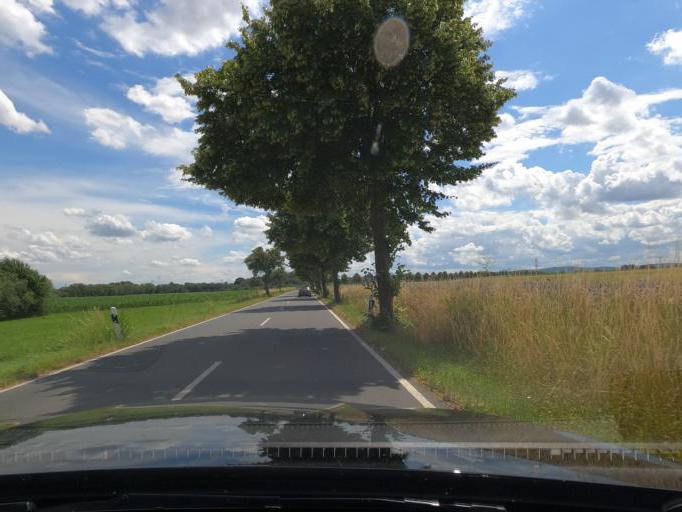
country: DE
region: Lower Saxony
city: Lengede
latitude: 52.1869
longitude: 10.3167
